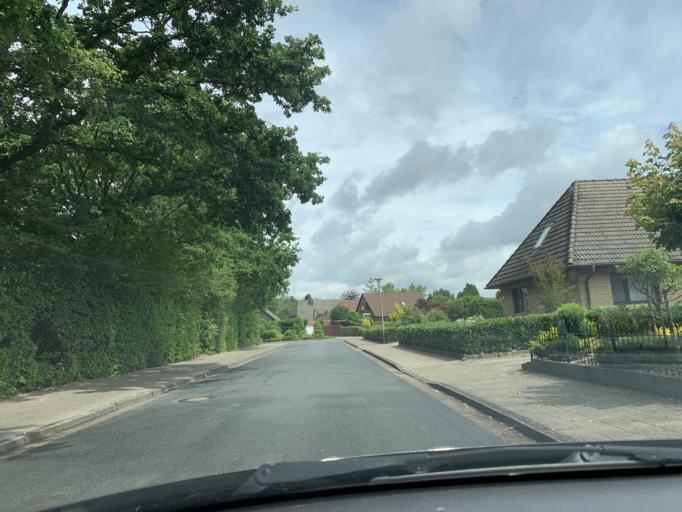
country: DE
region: Lower Saxony
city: Westerstede
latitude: 53.2548
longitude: 7.9382
